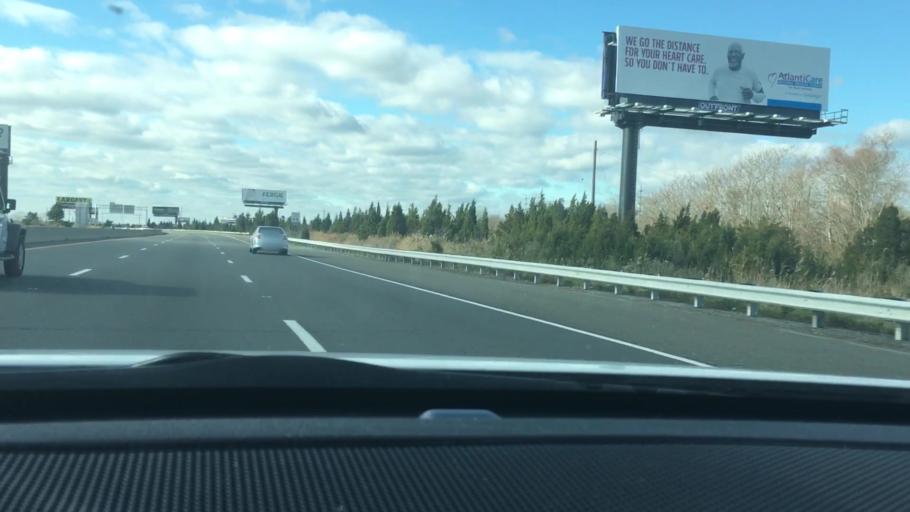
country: US
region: New Jersey
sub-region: Atlantic County
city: Atlantic City
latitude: 39.3660
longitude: -74.4533
